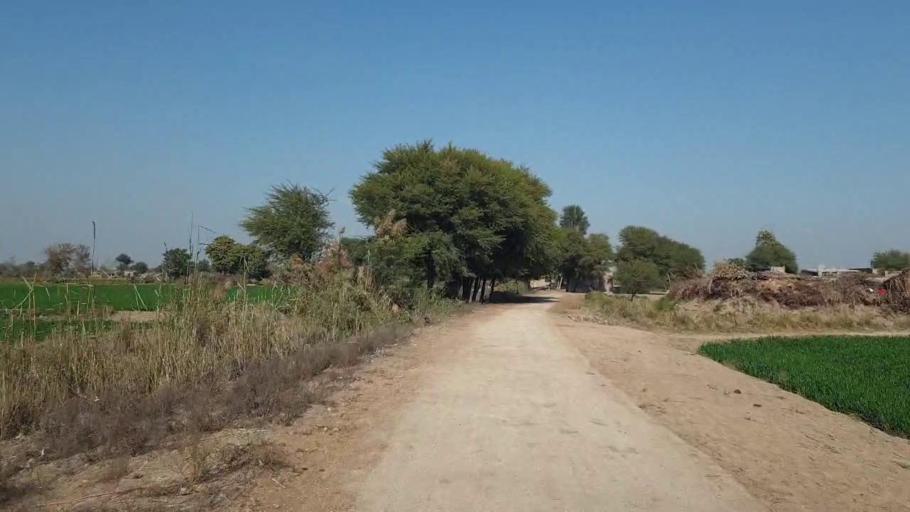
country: PK
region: Sindh
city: Shahdadpur
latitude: 25.9669
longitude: 68.6188
